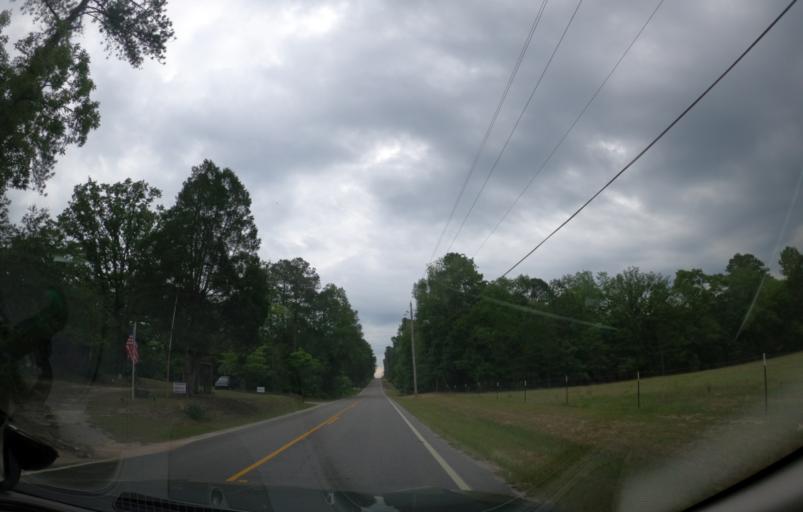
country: US
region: South Carolina
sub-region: Aiken County
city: Aiken
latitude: 33.5687
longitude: -81.6487
